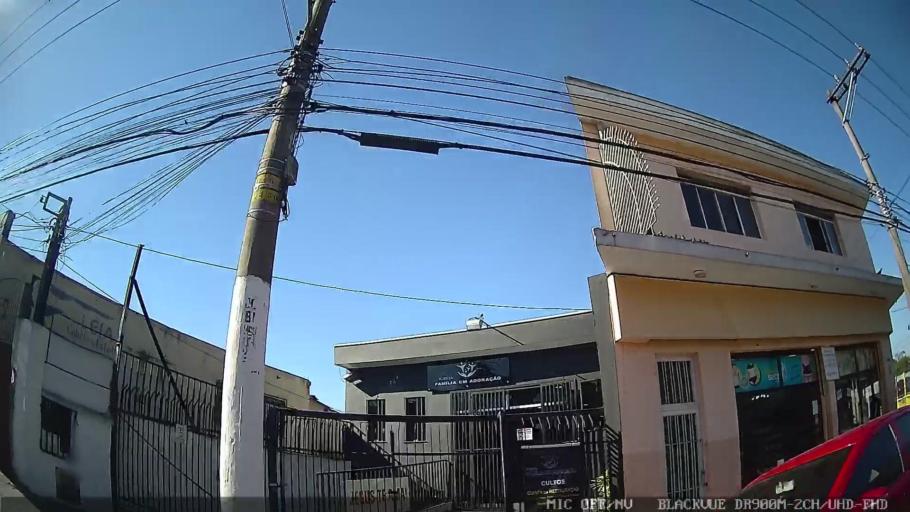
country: BR
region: Sao Paulo
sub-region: Sao Caetano Do Sul
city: Sao Caetano do Sul
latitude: -23.5480
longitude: -46.5100
